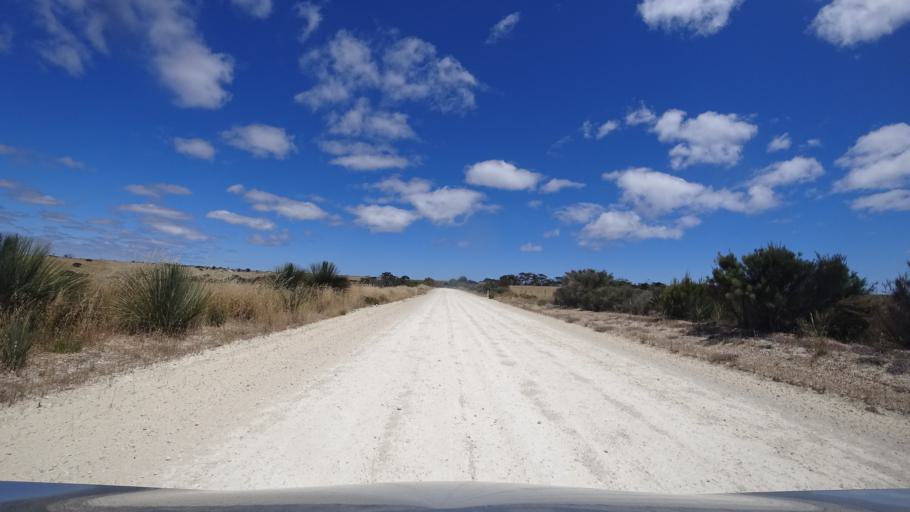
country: AU
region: South Australia
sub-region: Kangaroo Island
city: Kingscote
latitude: -35.6461
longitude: 137.3598
